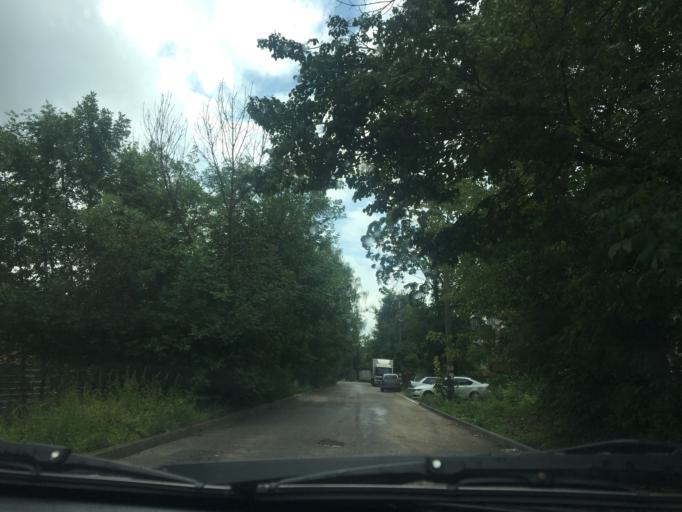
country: RU
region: Tula
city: Mendeleyevskiy
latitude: 54.1523
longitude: 37.5918
